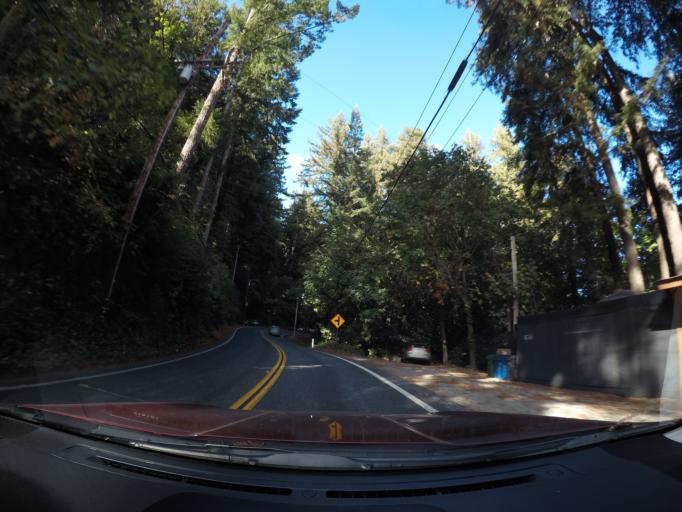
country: US
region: California
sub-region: Santa Cruz County
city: Ben Lomond
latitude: 37.0820
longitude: -122.0858
